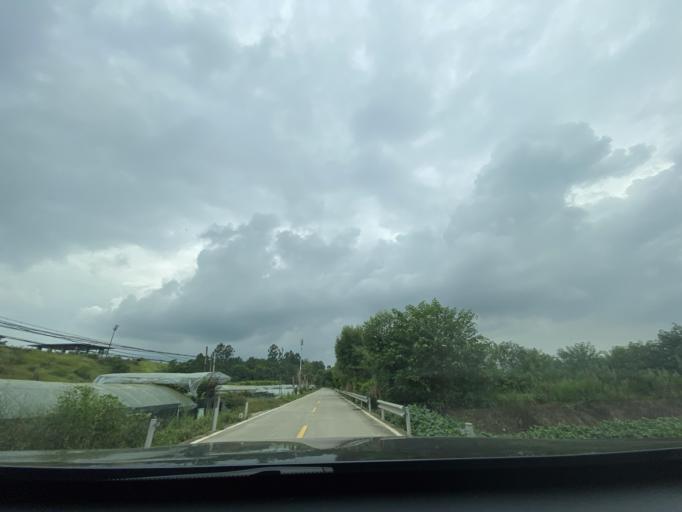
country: CN
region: Sichuan
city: Wujin
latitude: 30.3906
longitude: 103.9670
